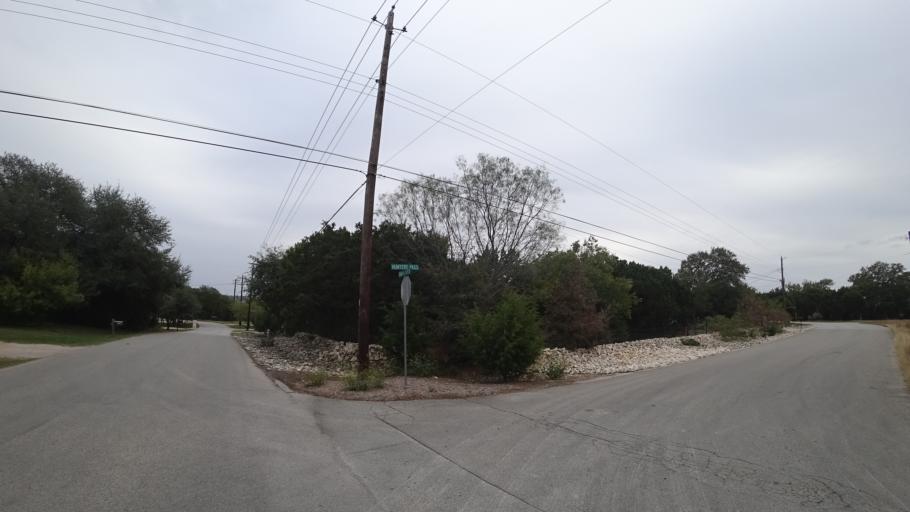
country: US
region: Texas
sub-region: Travis County
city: Hudson Bend
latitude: 30.3740
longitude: -97.9244
